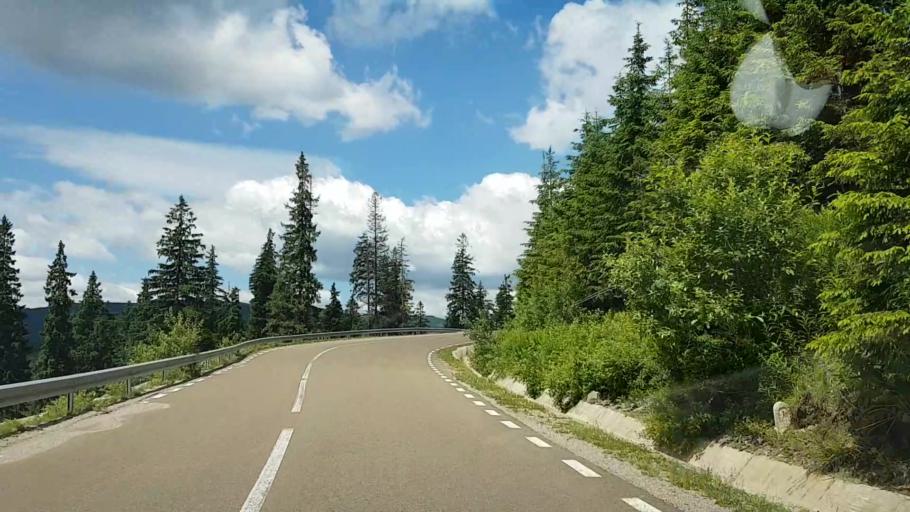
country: RO
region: Suceava
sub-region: Comuna Sadova
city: Sadova
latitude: 47.4593
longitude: 25.5260
